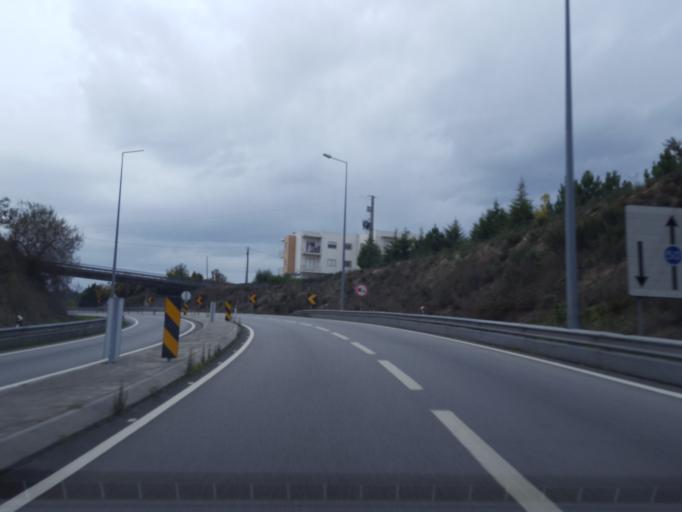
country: PT
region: Porto
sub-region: Marco de Canaveses
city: Marco de Canavezes
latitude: 41.2100
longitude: -8.1656
